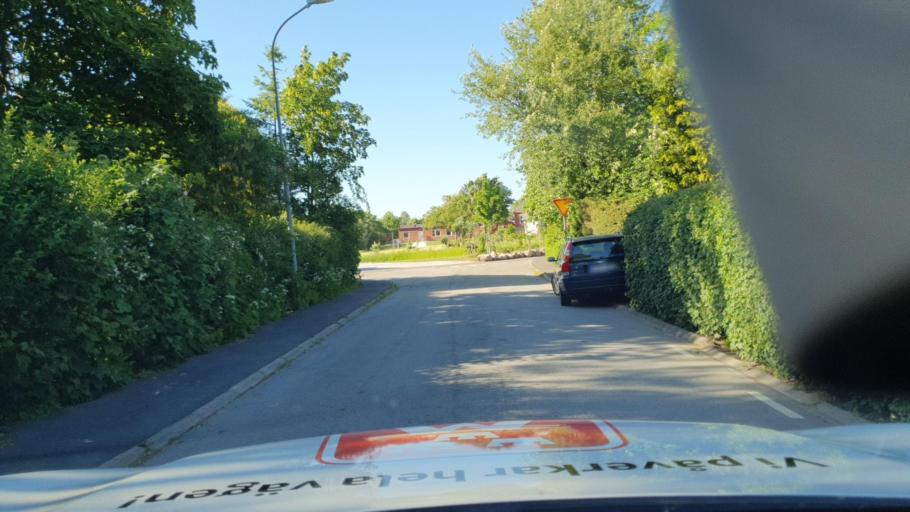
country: SE
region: Skane
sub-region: Skurups Kommun
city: Rydsgard
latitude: 55.5100
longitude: 13.5481
